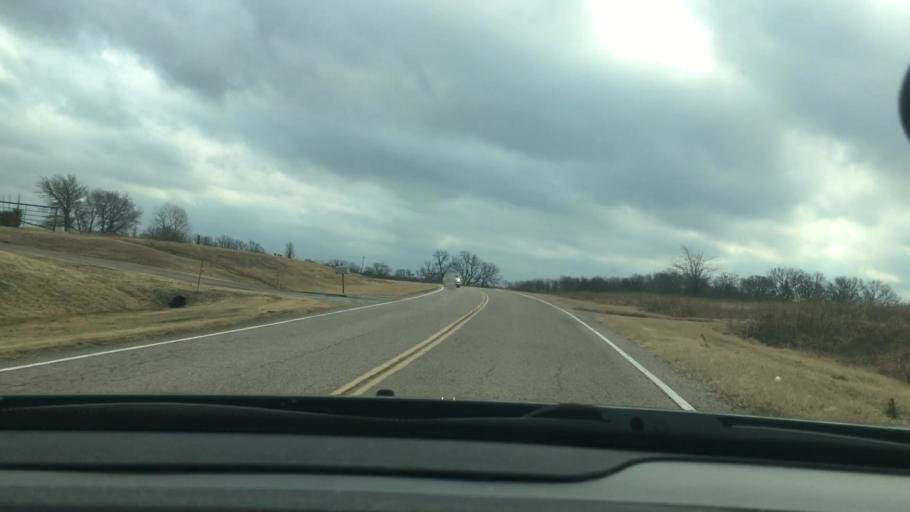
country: US
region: Oklahoma
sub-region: Bryan County
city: Durant
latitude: 34.0820
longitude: -96.3776
